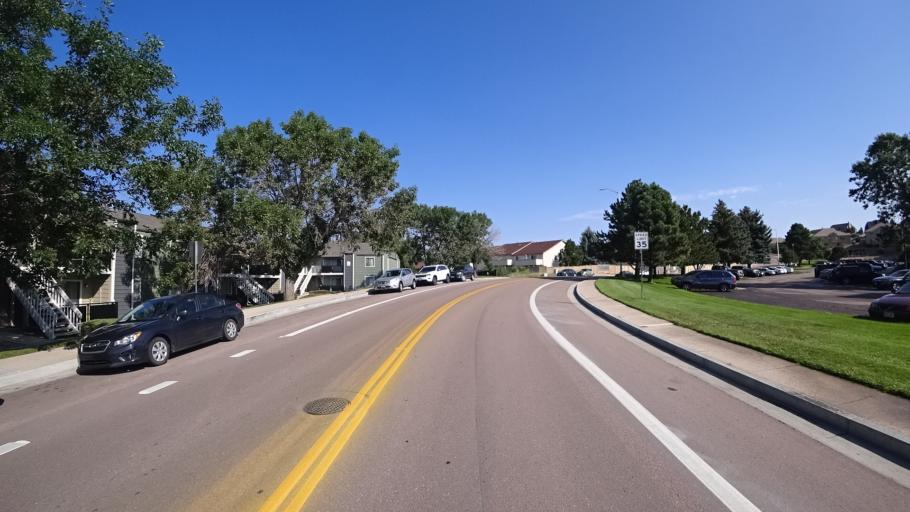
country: US
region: Colorado
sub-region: El Paso County
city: Air Force Academy
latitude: 38.9494
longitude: -104.7887
